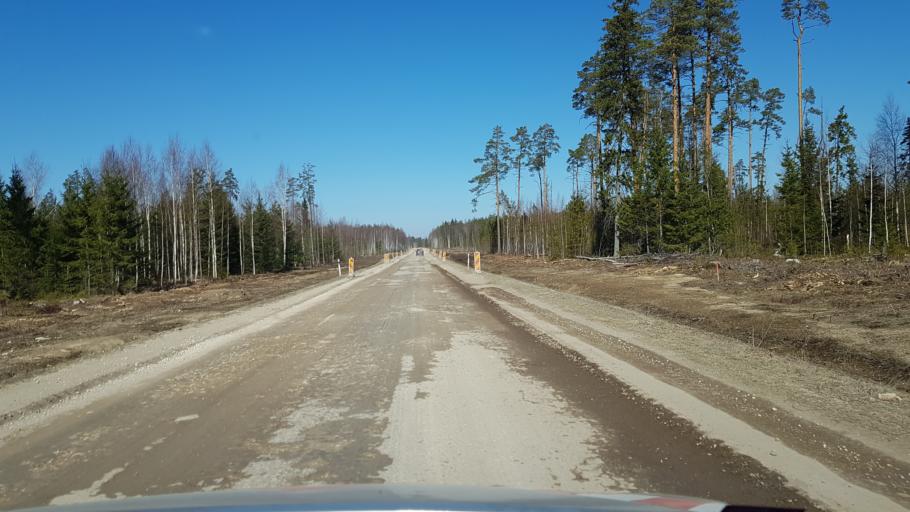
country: EE
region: Laeaene-Virumaa
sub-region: Vinni vald
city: Vinni
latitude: 59.0465
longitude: 26.6597
